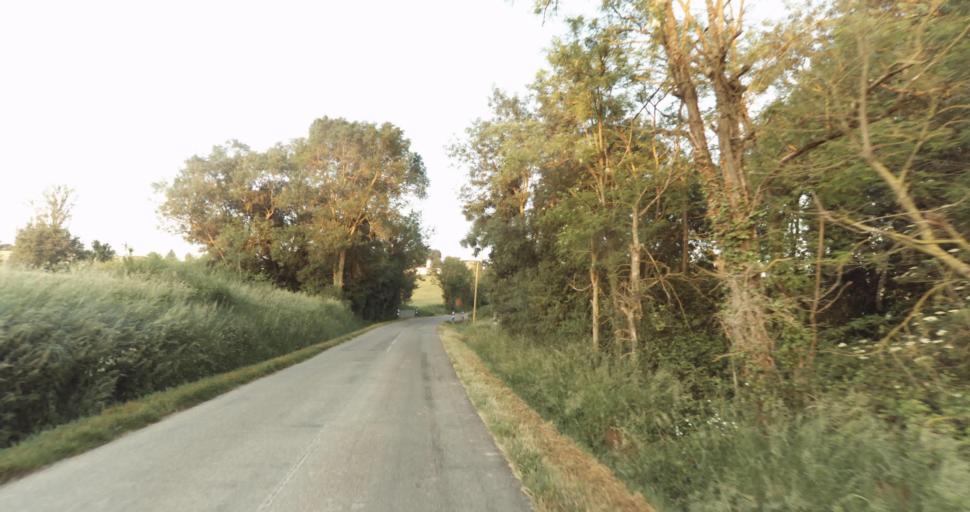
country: FR
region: Midi-Pyrenees
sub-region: Departement du Gers
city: Pujaudran
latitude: 43.6533
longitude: 1.1082
